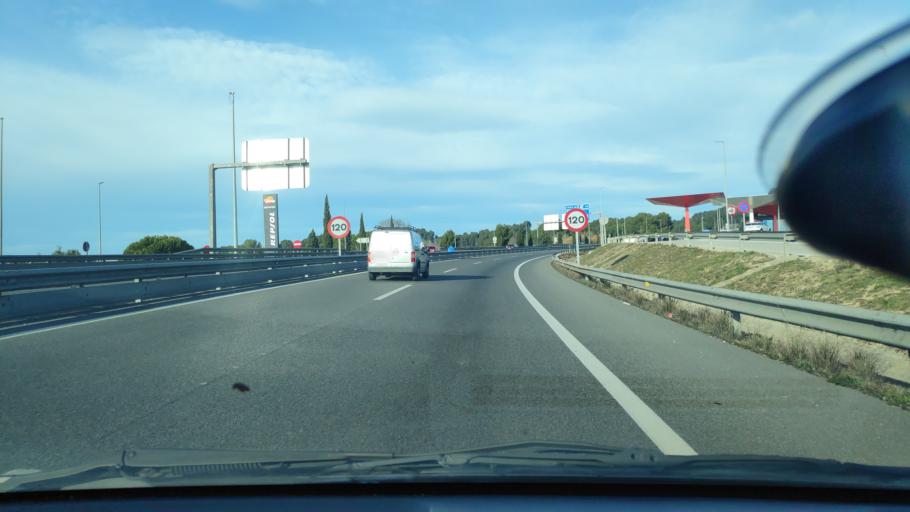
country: ES
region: Catalonia
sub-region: Provincia de Barcelona
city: Rubi
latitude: 41.4972
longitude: 2.0489
